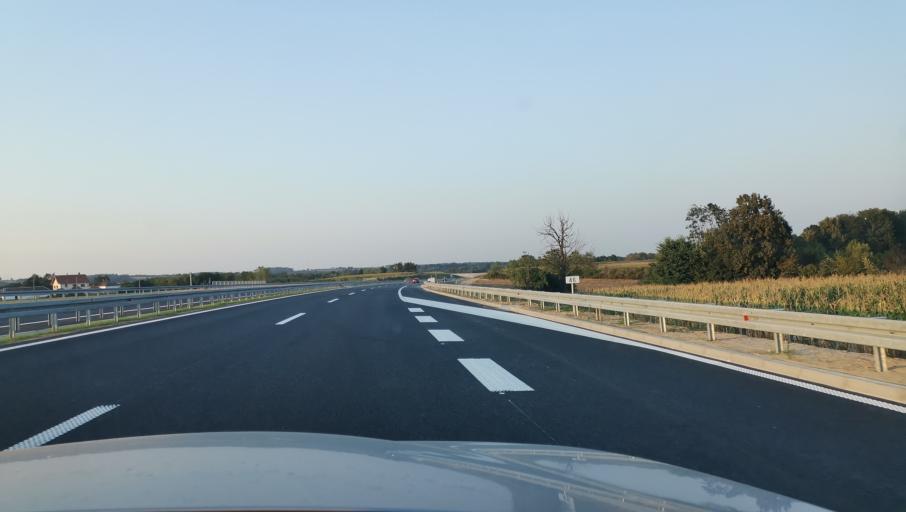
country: RS
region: Central Serbia
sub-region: Kolubarski Okrug
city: Ub
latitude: 44.4096
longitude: 20.0966
